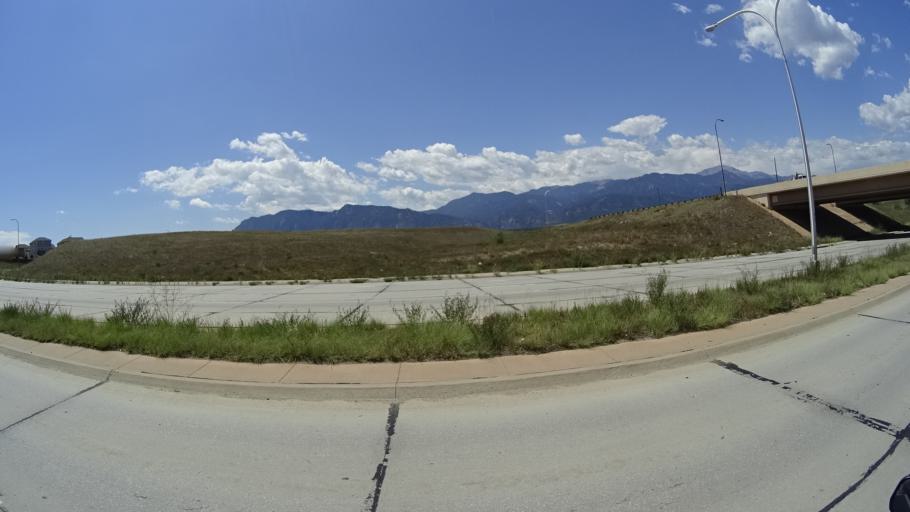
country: US
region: Colorado
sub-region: El Paso County
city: Stratmoor
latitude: 38.8116
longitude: -104.7887
